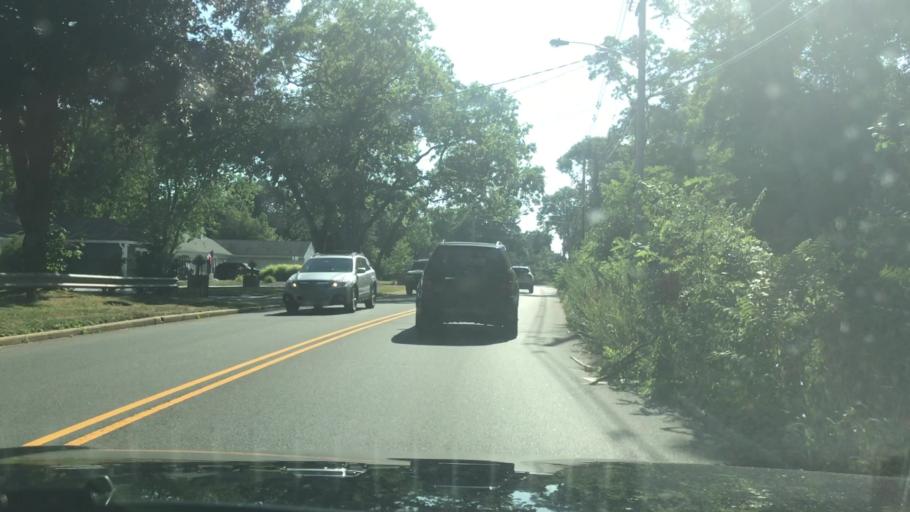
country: US
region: New Jersey
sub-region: Monmouth County
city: Red Bank
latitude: 40.3451
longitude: -74.0913
